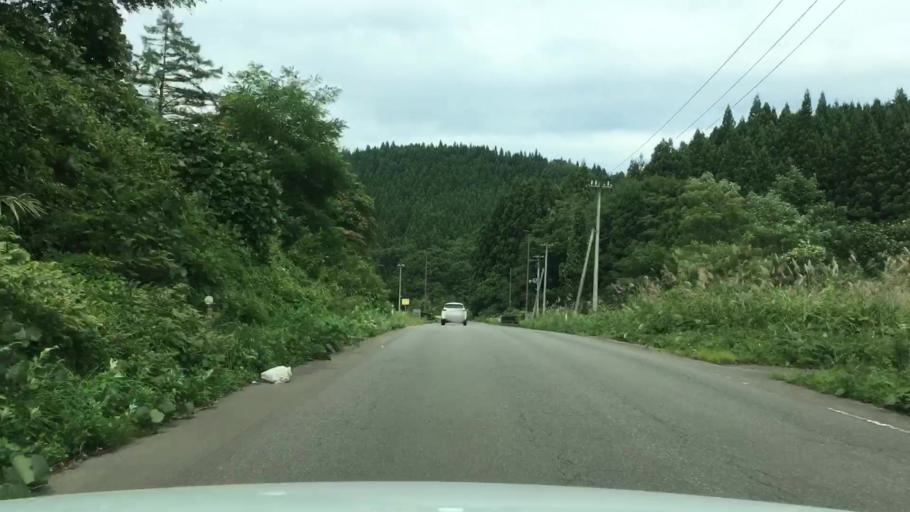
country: JP
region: Aomori
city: Shimokizukuri
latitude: 40.7449
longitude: 140.2411
